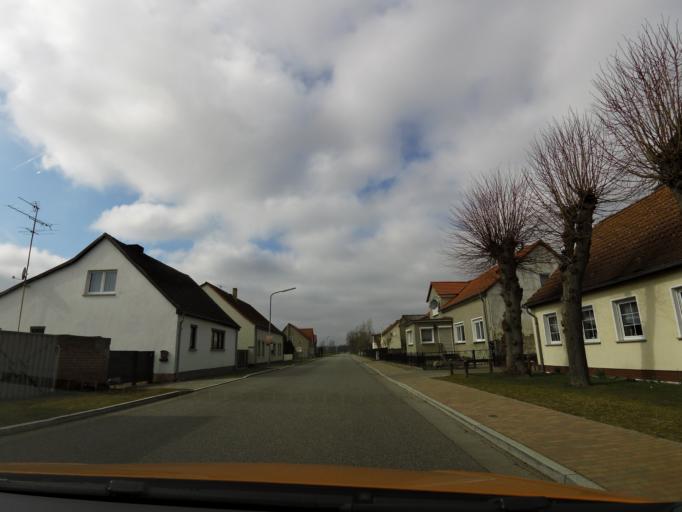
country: DE
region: Brandenburg
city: Rhinow
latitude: 52.7042
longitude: 12.3073
